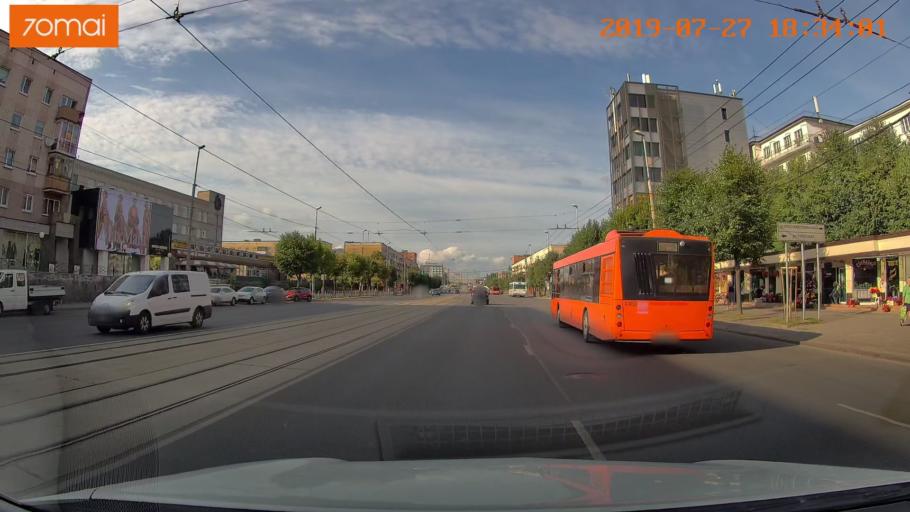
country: RU
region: Kaliningrad
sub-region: Gorod Kaliningrad
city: Kaliningrad
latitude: 54.7012
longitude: 20.5043
